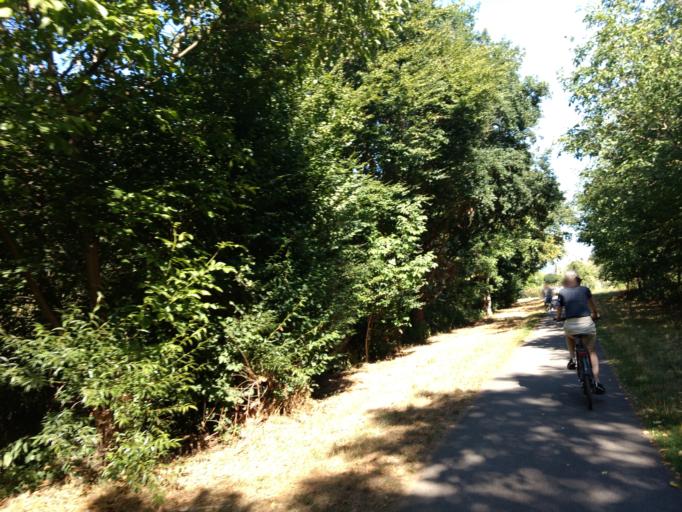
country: DE
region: Rheinland-Pfalz
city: Sinzig
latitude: 50.5488
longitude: 7.2382
